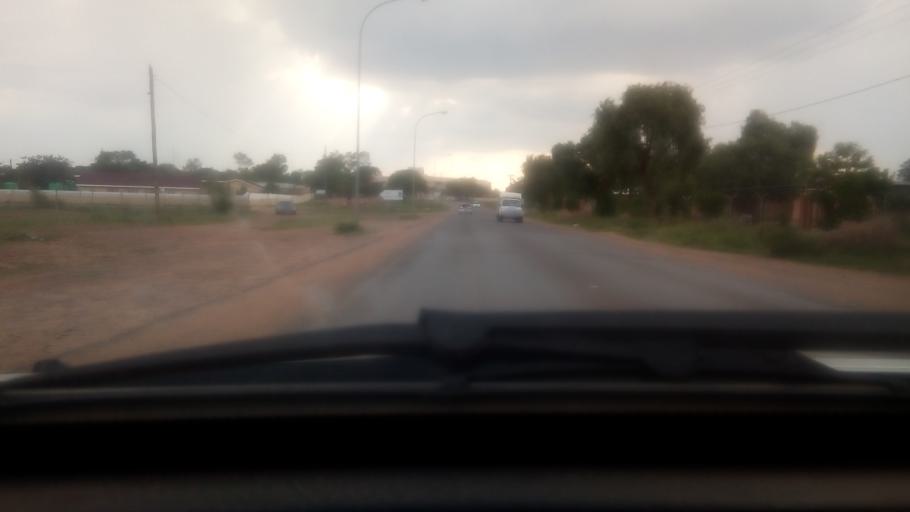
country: BW
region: Kweneng
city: Molepolole
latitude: -24.4109
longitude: 25.4916
